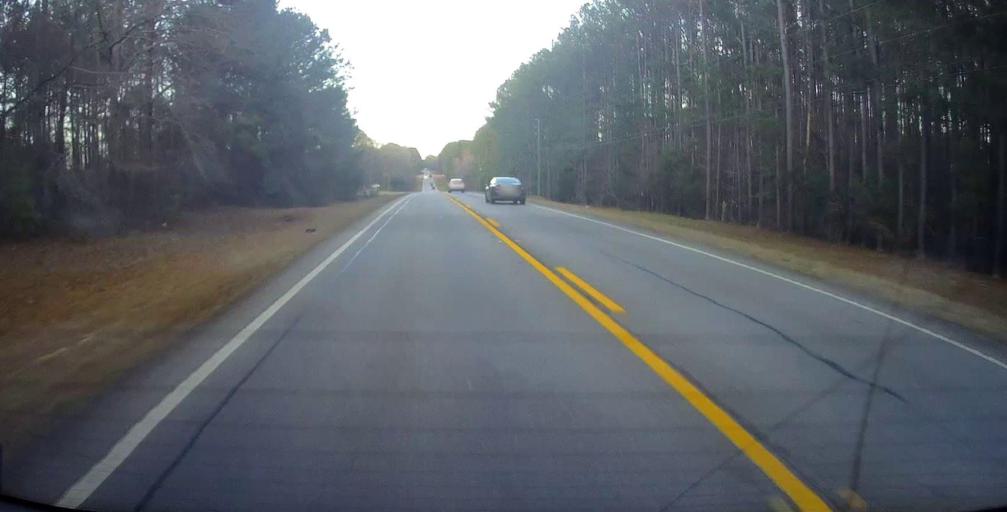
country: US
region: Georgia
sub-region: Harris County
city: Hamilton
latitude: 32.6392
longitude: -84.7890
